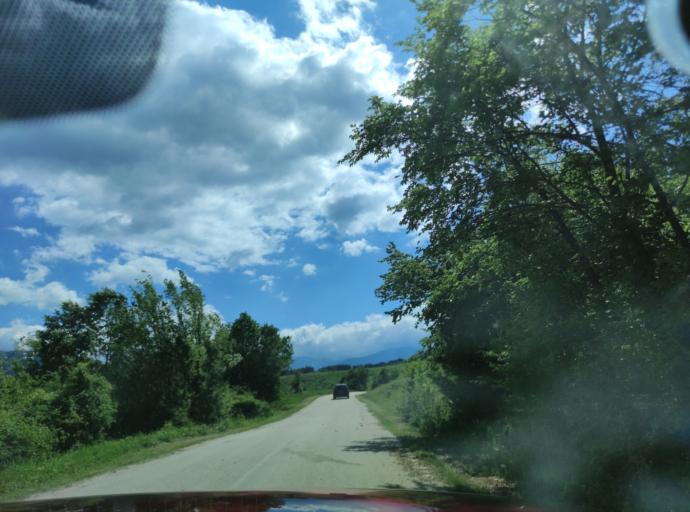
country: BG
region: Vidin
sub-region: Obshtina Ruzhintsi
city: Ruzhintsi
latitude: 43.5012
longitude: 22.7725
